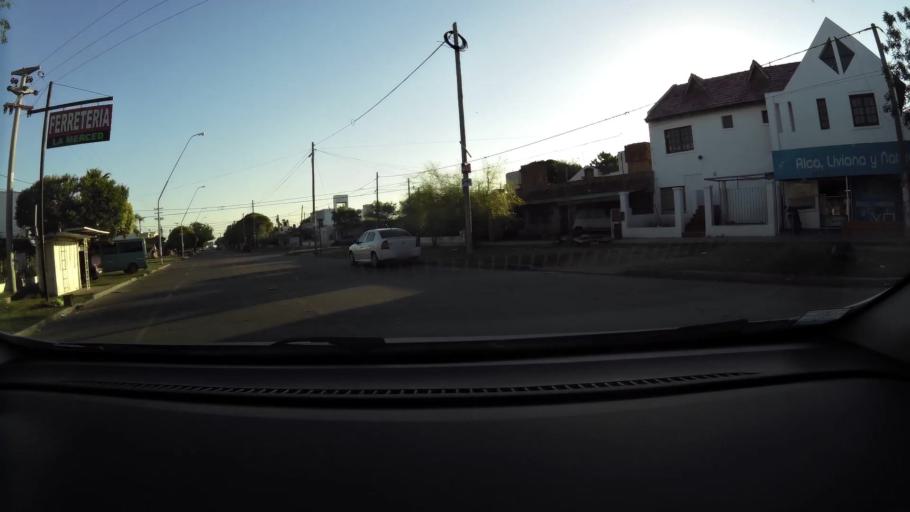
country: AR
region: Cordoba
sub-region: Departamento de Capital
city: Cordoba
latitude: -31.3747
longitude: -64.2138
